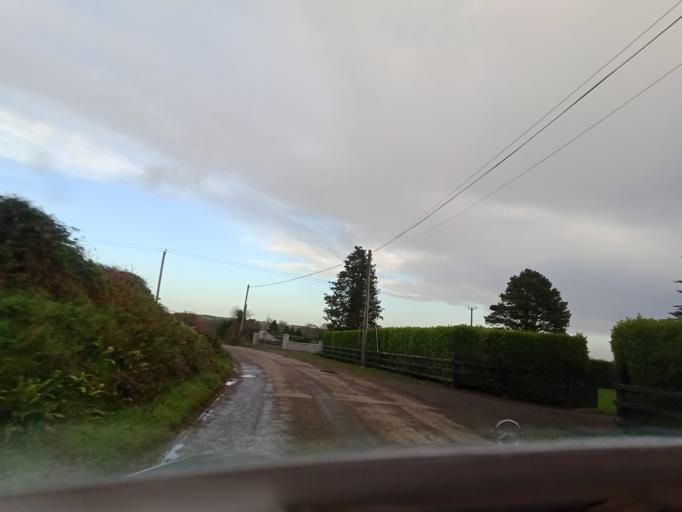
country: IE
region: Munster
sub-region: Waterford
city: Waterford
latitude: 52.3238
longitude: -7.0421
